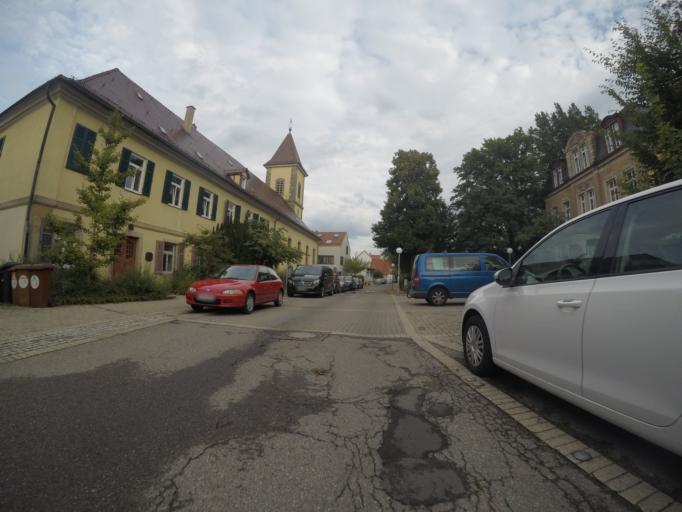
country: DE
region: Baden-Wuerttemberg
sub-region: Regierungsbezirk Stuttgart
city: Ostfildern
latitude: 48.7203
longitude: 9.2119
